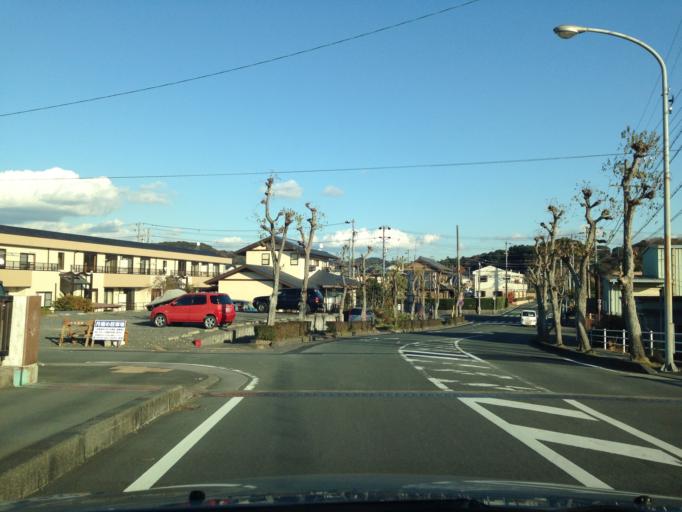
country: JP
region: Shizuoka
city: Fukuroi
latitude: 34.7355
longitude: 137.9365
